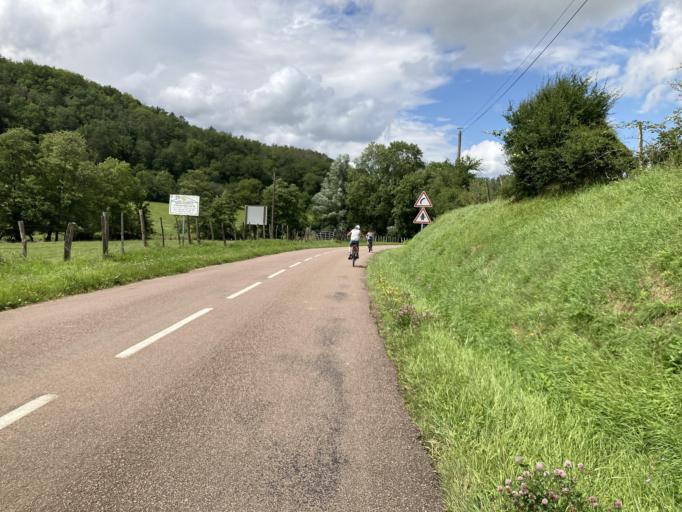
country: FR
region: Bourgogne
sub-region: Departement de la Cote-d'Or
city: Montbard
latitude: 47.6272
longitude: 4.3672
